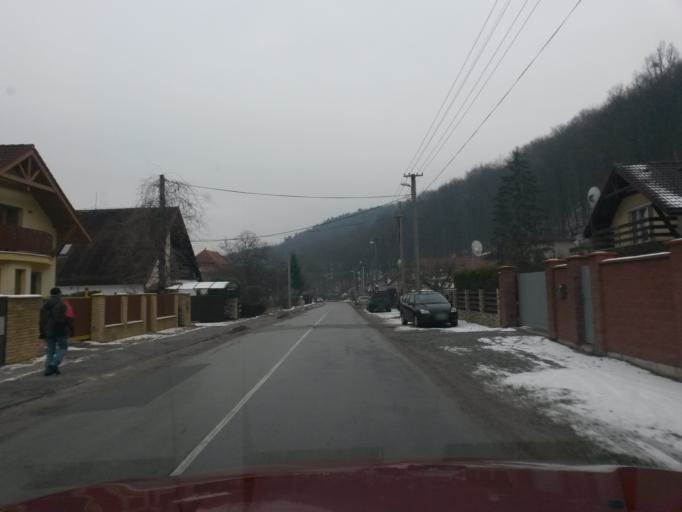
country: SK
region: Kosicky
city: Kosice
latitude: 48.7188
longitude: 21.1829
